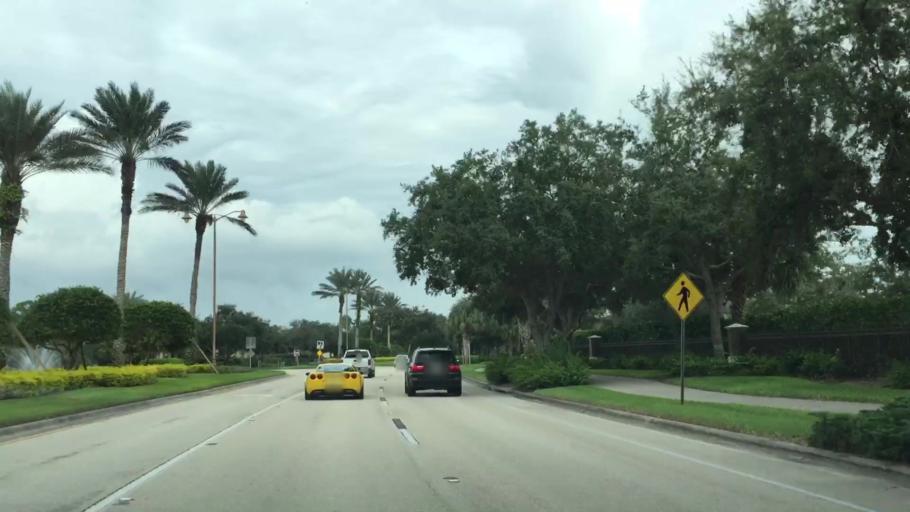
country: US
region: Florida
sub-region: Lee County
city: Estero
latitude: 26.3989
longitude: -81.7996
